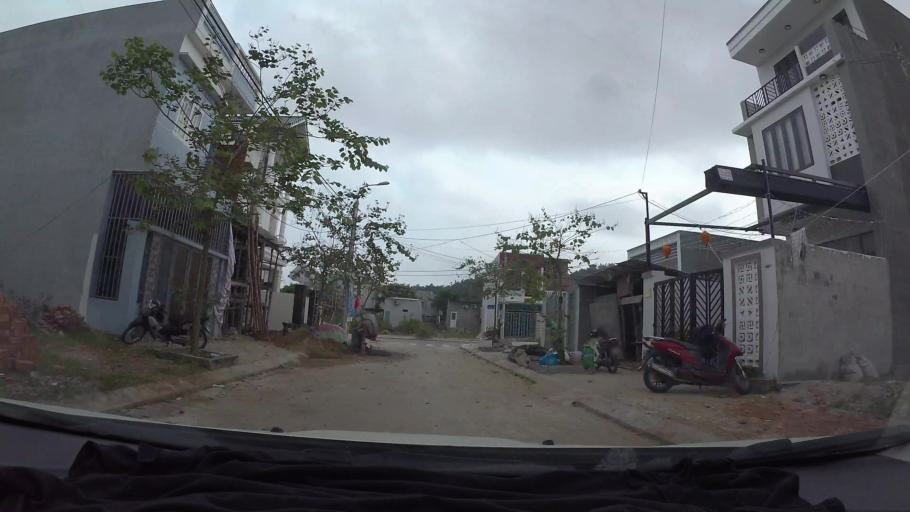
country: VN
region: Da Nang
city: Cam Le
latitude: 16.0379
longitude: 108.1747
